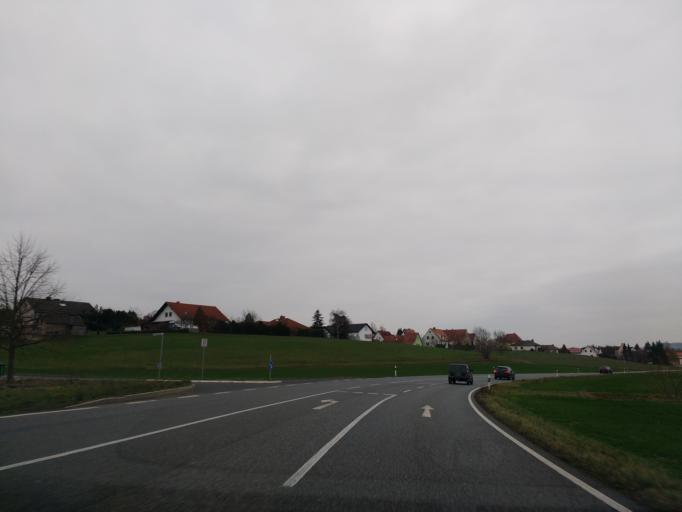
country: DE
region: Hesse
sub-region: Regierungsbezirk Kassel
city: Alheim
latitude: 51.0533
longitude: 9.6598
